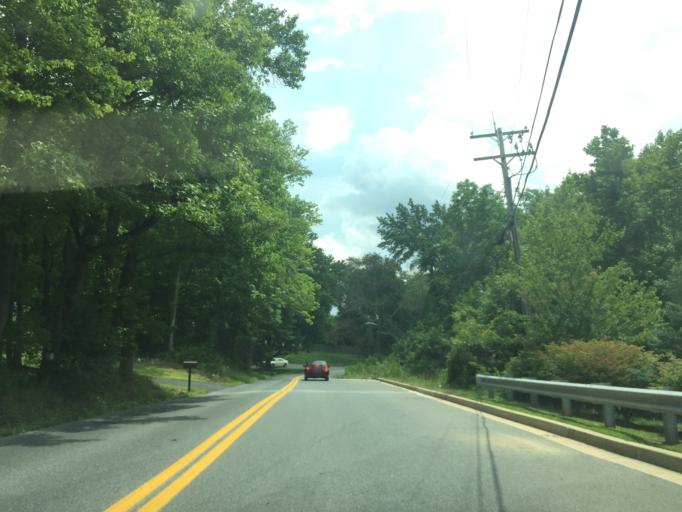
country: US
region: Maryland
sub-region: Baltimore County
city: White Marsh
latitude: 39.3943
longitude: -76.4281
